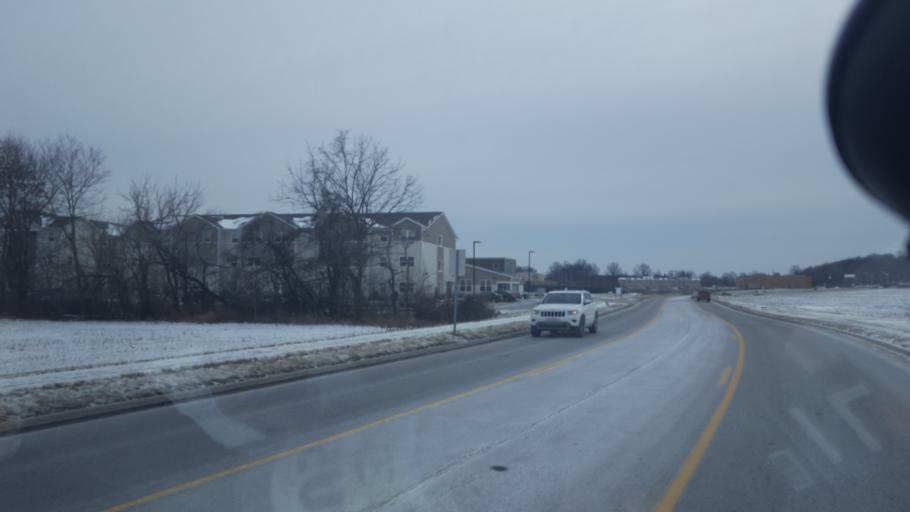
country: US
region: Ohio
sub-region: Marion County
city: Marion
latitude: 40.5857
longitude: -83.0914
